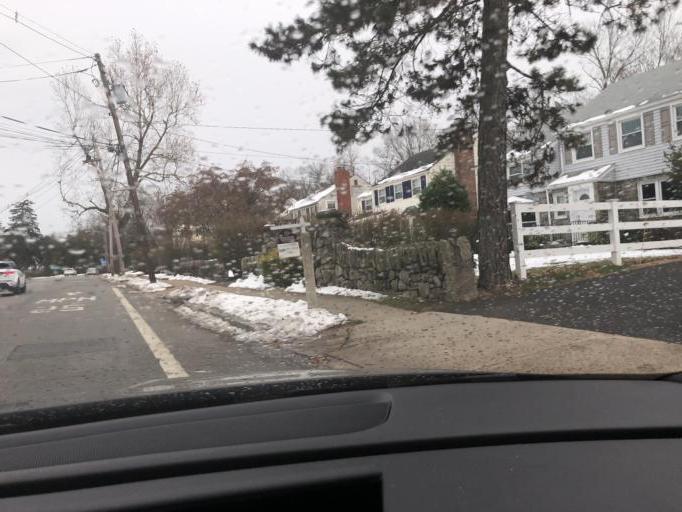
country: US
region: New Jersey
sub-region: Morris County
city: Morristown
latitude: 40.7963
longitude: -74.4606
